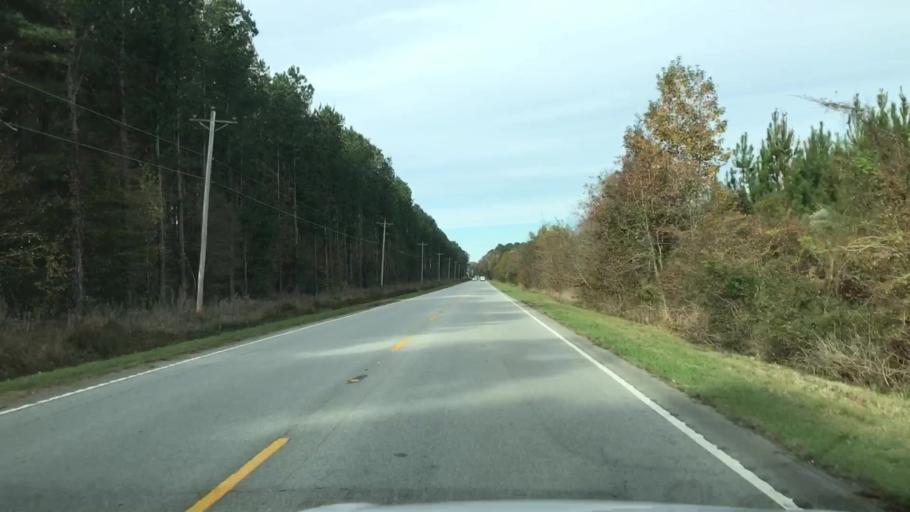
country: US
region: South Carolina
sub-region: Colleton County
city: Walterboro
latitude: 32.8175
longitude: -80.5430
